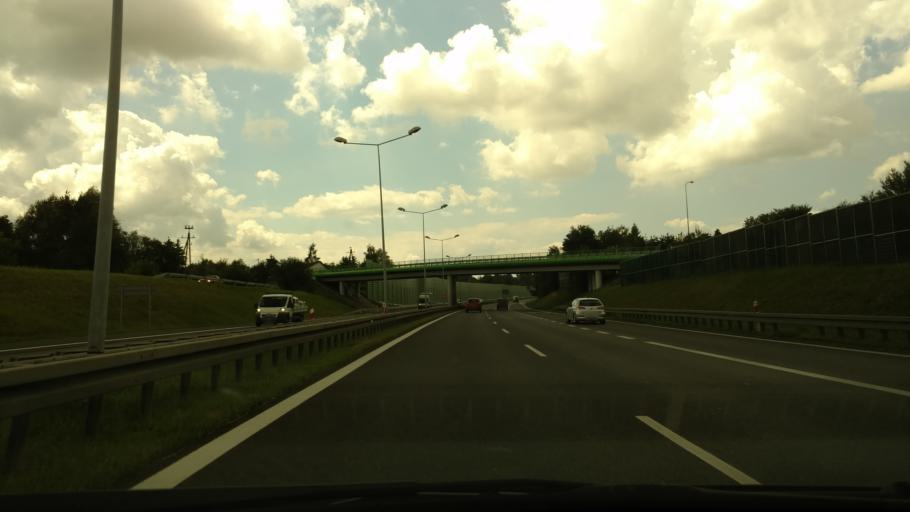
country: PL
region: Lesser Poland Voivodeship
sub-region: Powiat krakowski
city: Rzaska
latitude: 50.1040
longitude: 19.8372
